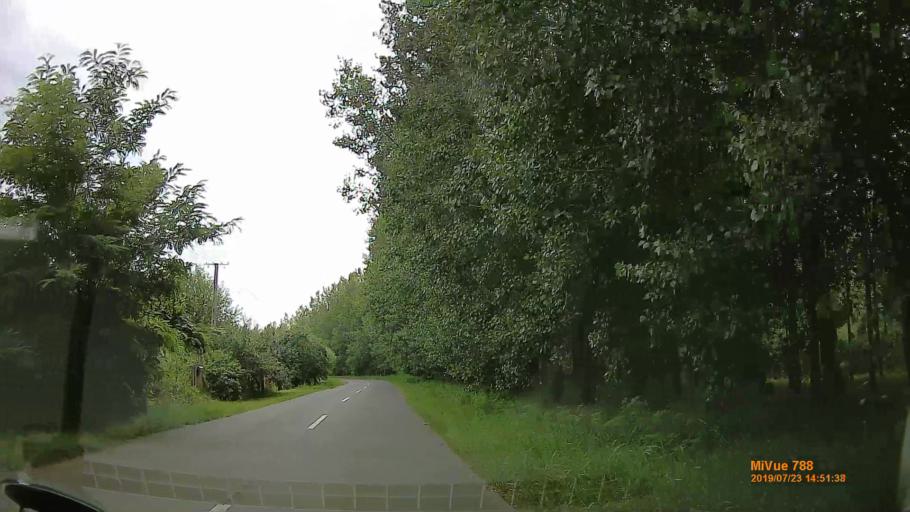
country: HU
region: Szabolcs-Szatmar-Bereg
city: Kalmanhaza
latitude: 47.8812
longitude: 21.6525
